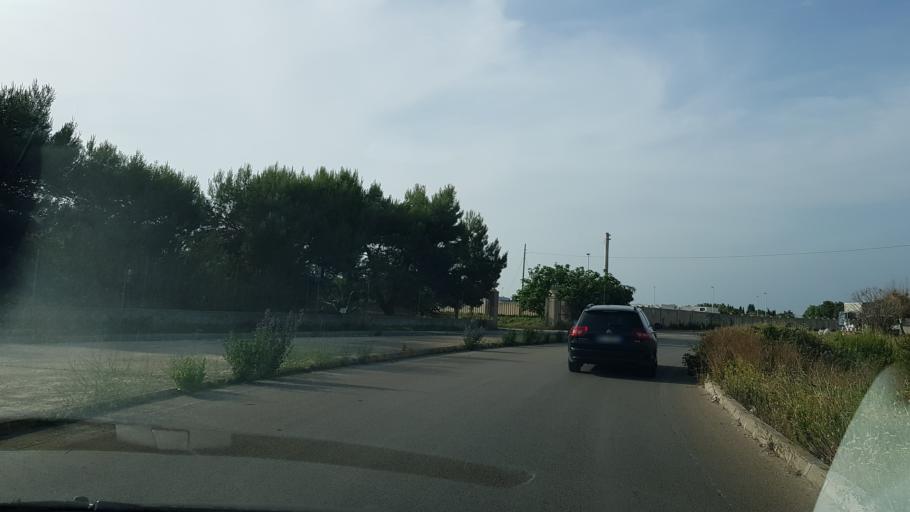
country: IT
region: Apulia
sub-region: Provincia di Lecce
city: Porto Cesareo
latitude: 40.2956
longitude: 17.8558
